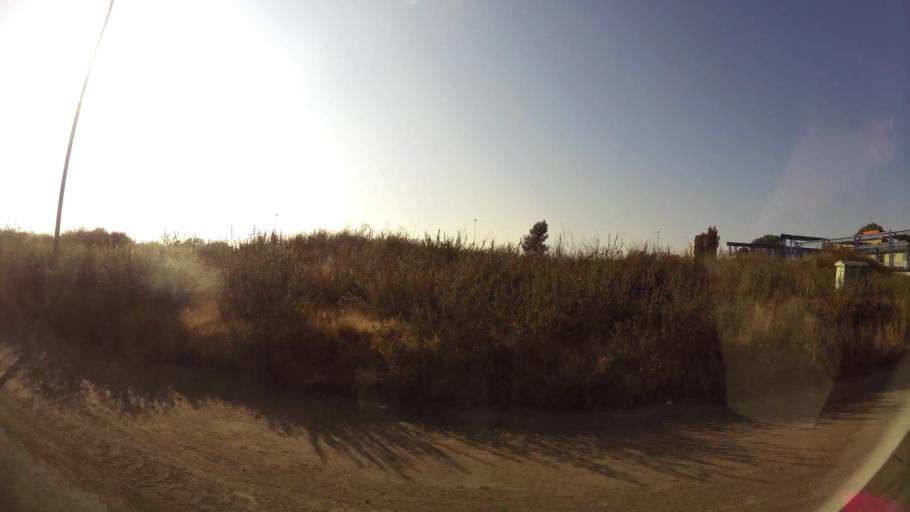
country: ZA
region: Orange Free State
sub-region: Mangaung Metropolitan Municipality
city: Bloemfontein
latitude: -29.1286
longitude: 26.2661
